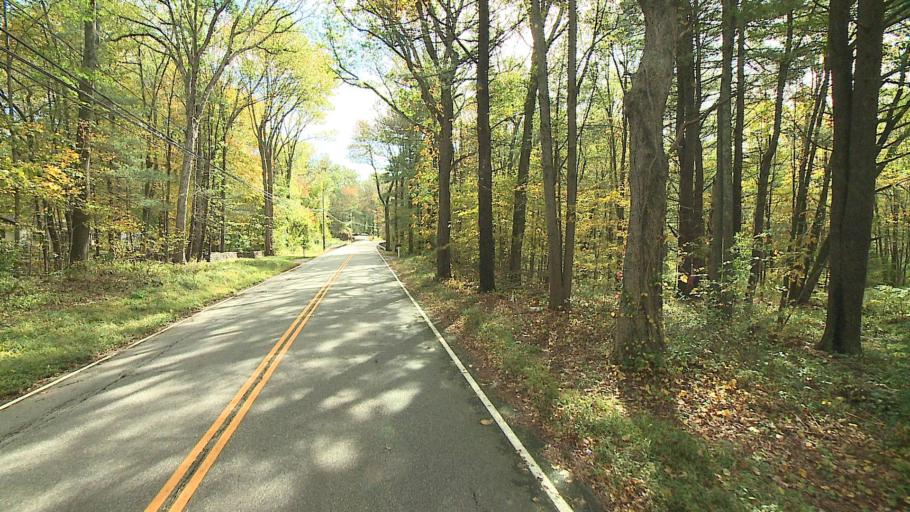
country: US
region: Connecticut
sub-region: Windham County
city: Putnam
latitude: 41.8849
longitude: -71.8754
